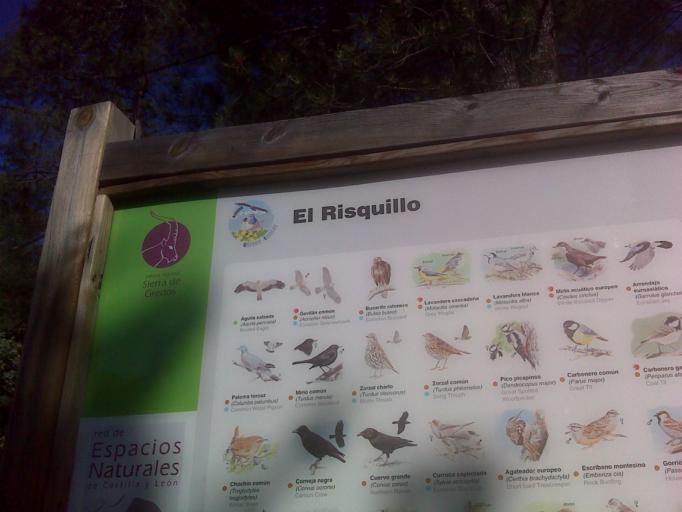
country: ES
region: Castille and Leon
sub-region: Provincia de Avila
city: Guisando
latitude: 40.2214
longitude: -5.1445
